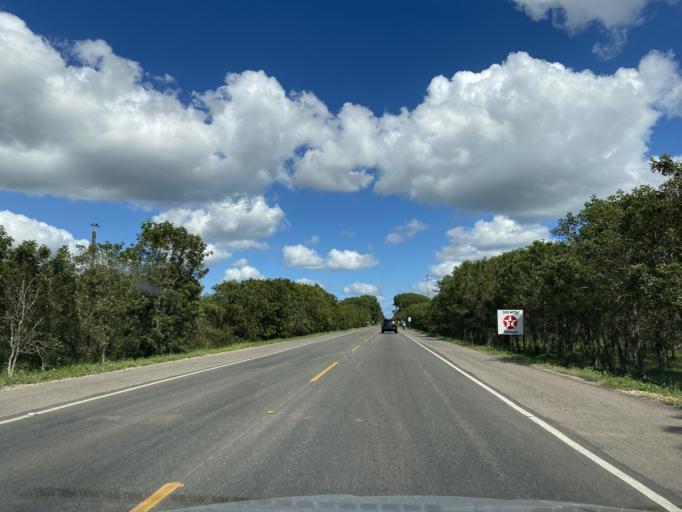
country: DO
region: Monte Plata
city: Monte Plata
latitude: 18.7643
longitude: -69.7596
